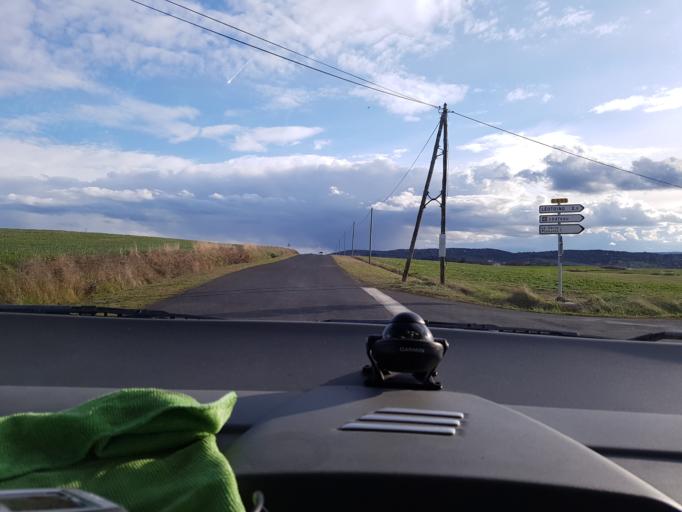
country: FR
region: Auvergne
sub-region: Departement de la Haute-Loire
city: Lempdes-sur-Allagnon
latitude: 45.3594
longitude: 3.2494
